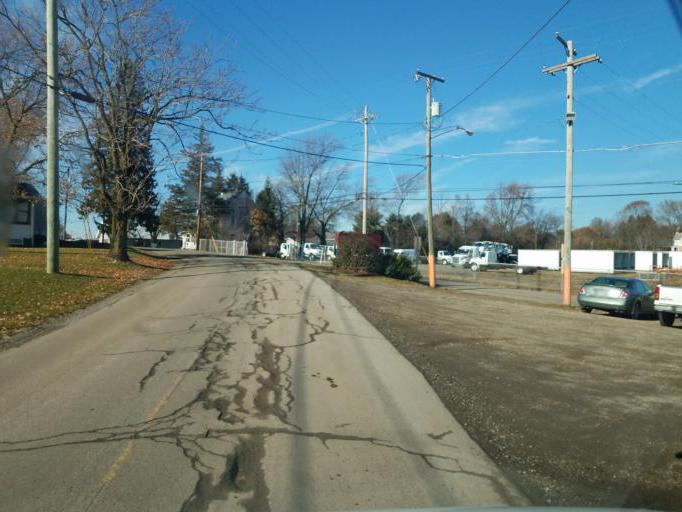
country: US
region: Ohio
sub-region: Wayne County
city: Dalton
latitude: 40.7410
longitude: -81.7427
